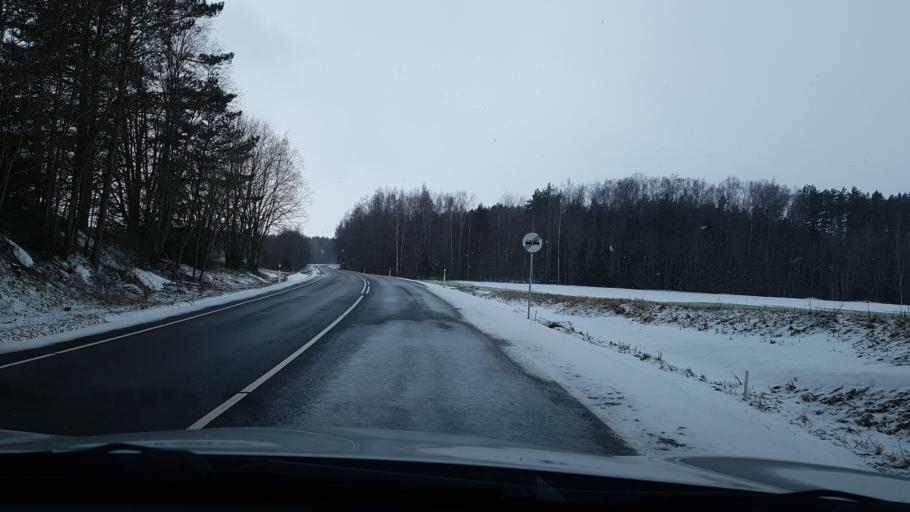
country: EE
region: Polvamaa
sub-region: Polva linn
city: Polva
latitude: 58.0916
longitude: 27.1315
